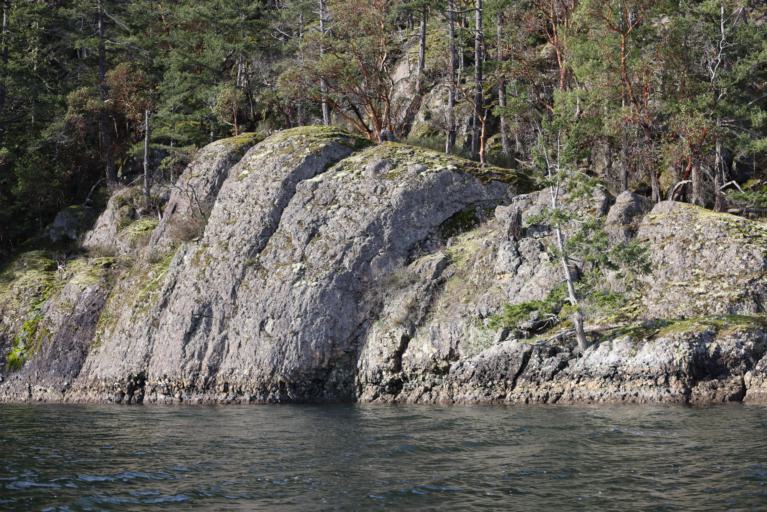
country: CA
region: British Columbia
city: North Cowichan
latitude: 48.7956
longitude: -123.5616
